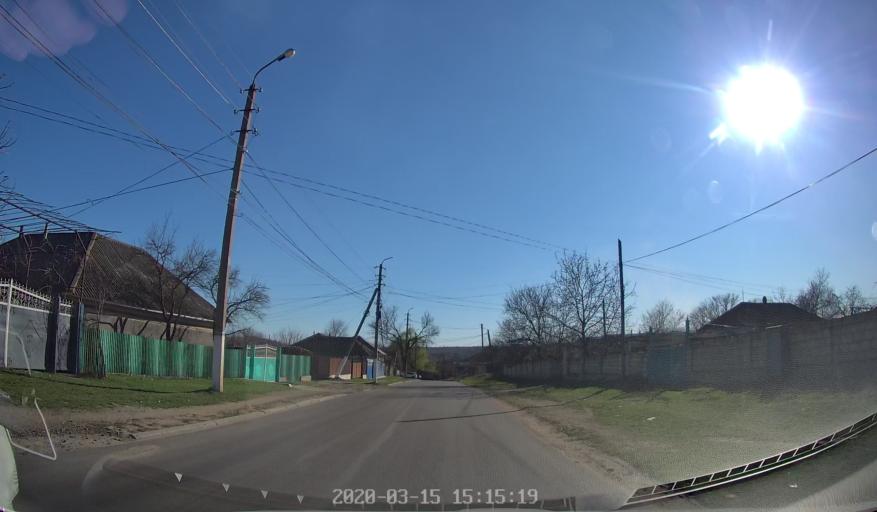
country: MD
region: Chisinau
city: Cricova
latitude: 47.2428
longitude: 28.7643
